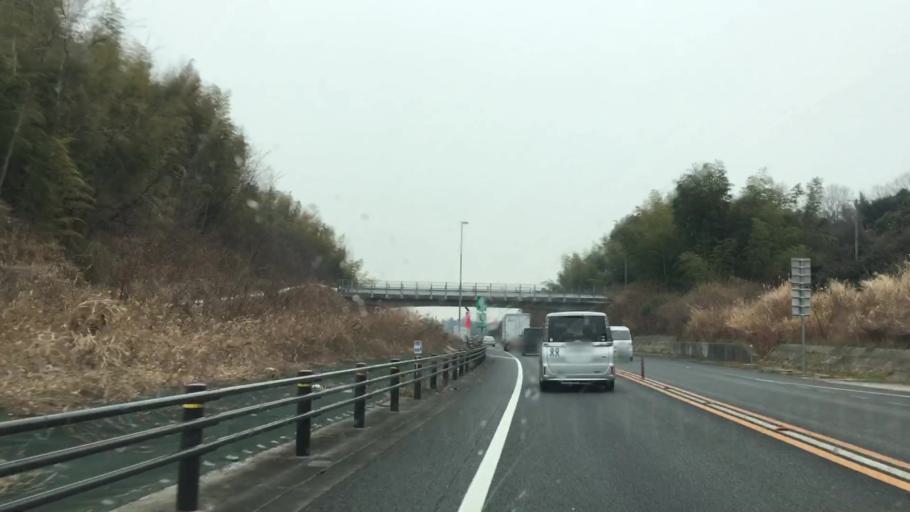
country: JP
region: Aichi
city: Nishio
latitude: 34.8508
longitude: 137.1320
